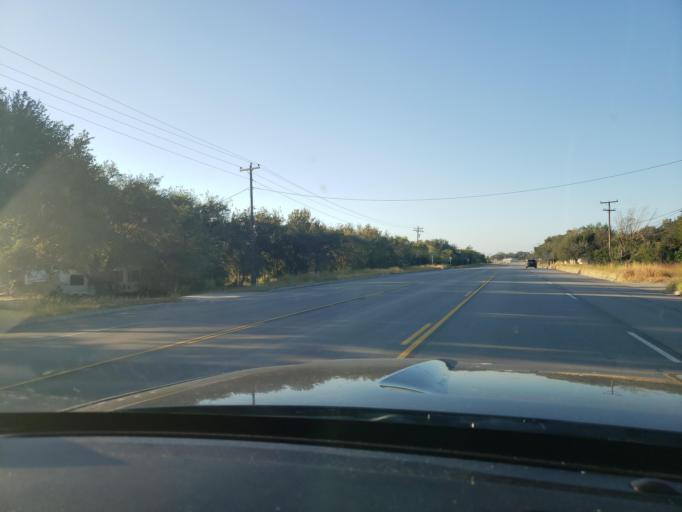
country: US
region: Texas
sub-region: Bee County
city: Beeville
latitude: 28.4258
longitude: -97.7165
